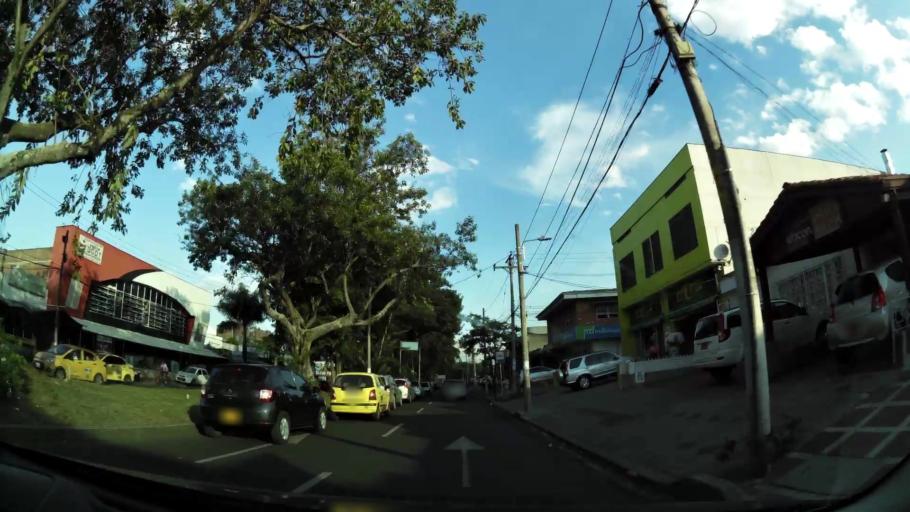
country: CO
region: Valle del Cauca
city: Cali
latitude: 3.4788
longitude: -76.5185
